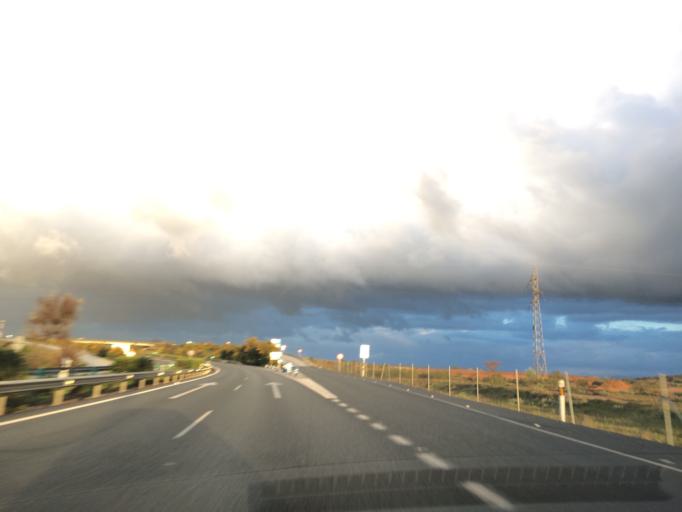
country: ES
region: Andalusia
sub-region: Provincia de Sevilla
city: Alcala de Guadaira
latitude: 37.3273
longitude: -5.8096
